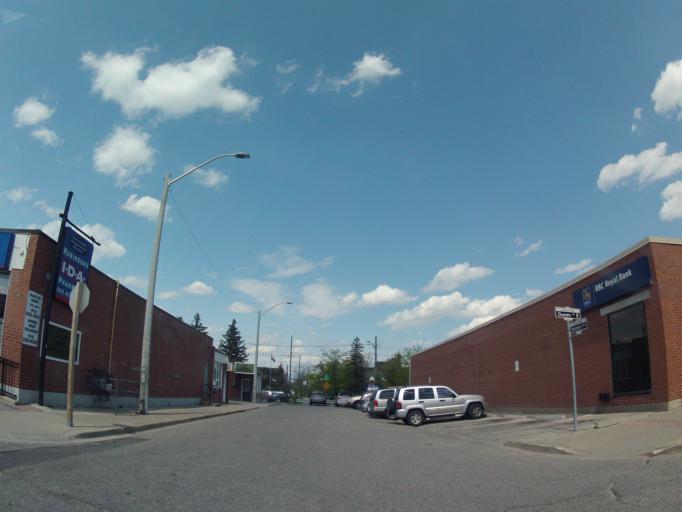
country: CA
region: Ontario
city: Mississauga
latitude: 43.5818
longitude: -79.7138
